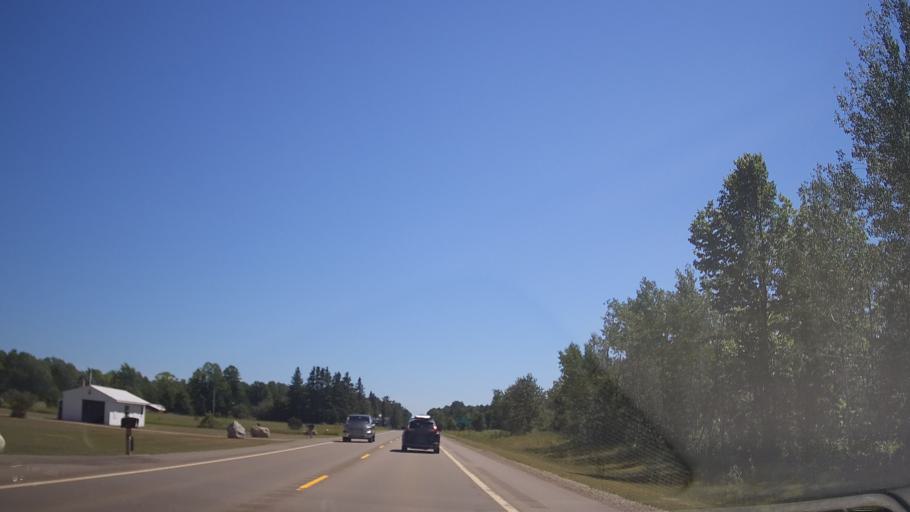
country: US
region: Michigan
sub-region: Cheboygan County
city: Indian River
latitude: 45.5973
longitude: -84.7826
